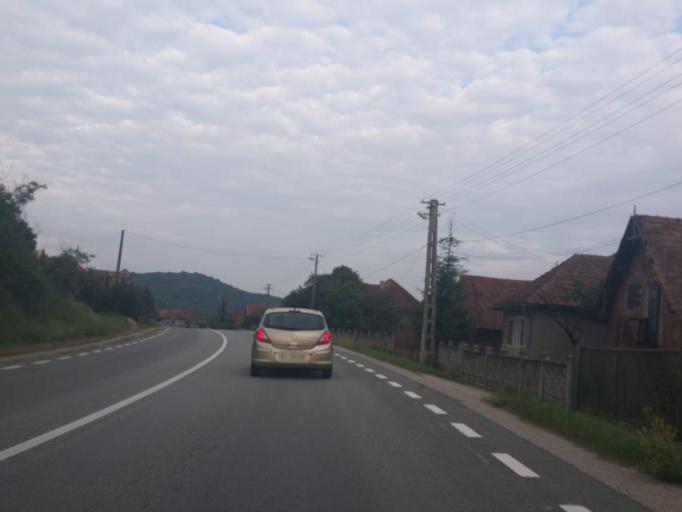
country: RO
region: Salaj
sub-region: Comuna Sanmihaiu Almasului
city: Sanmihaiu Almasului
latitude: 46.9577
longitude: 23.3356
